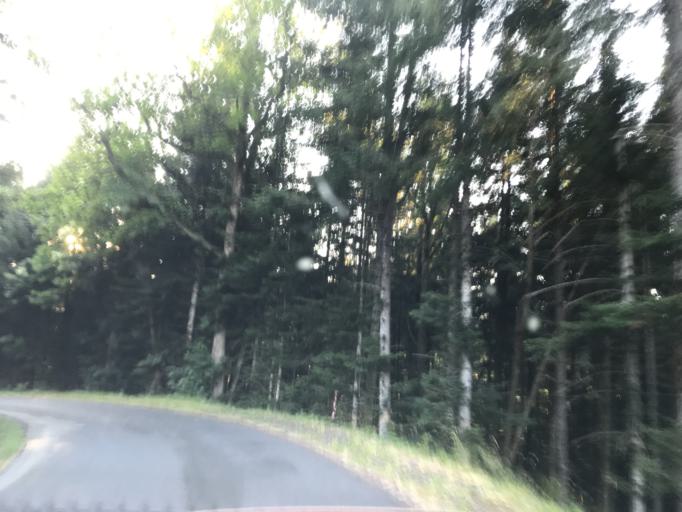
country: FR
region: Auvergne
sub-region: Departement du Puy-de-Dome
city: Courpiere
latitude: 45.7566
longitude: 3.6287
